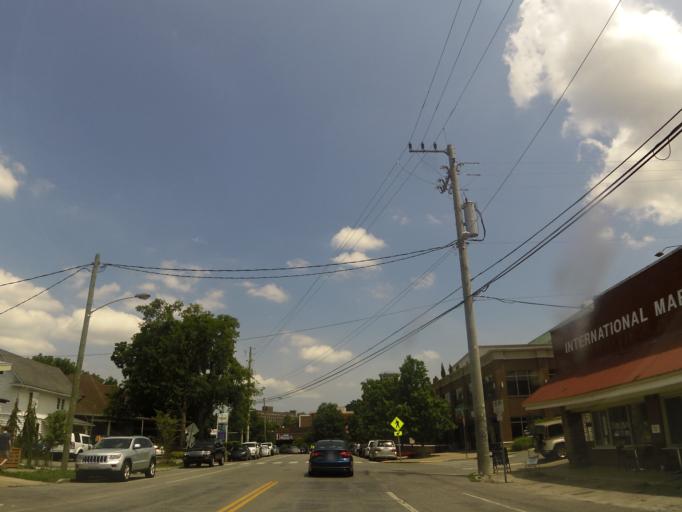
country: US
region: Tennessee
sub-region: Davidson County
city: Nashville
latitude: 36.1316
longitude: -86.7955
